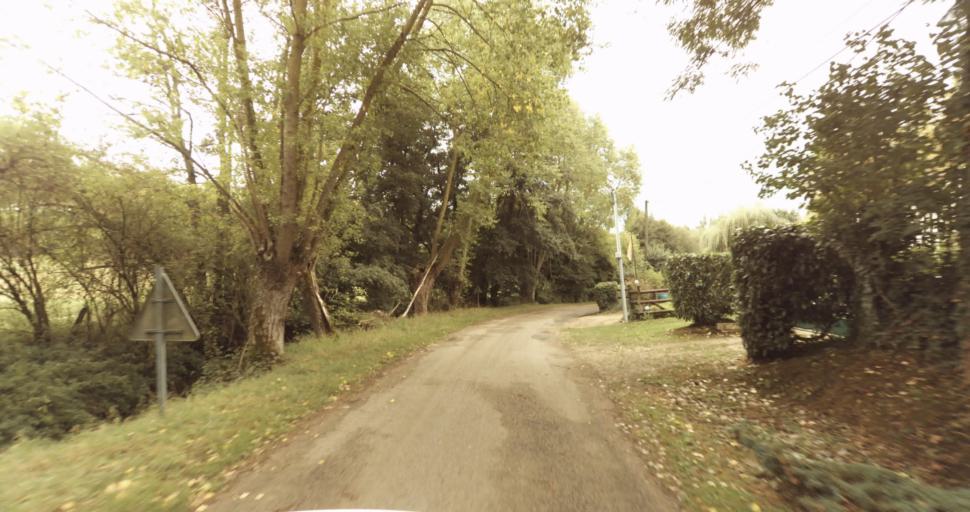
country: FR
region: Lower Normandy
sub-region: Departement de l'Orne
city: Trun
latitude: 48.9245
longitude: 0.0868
